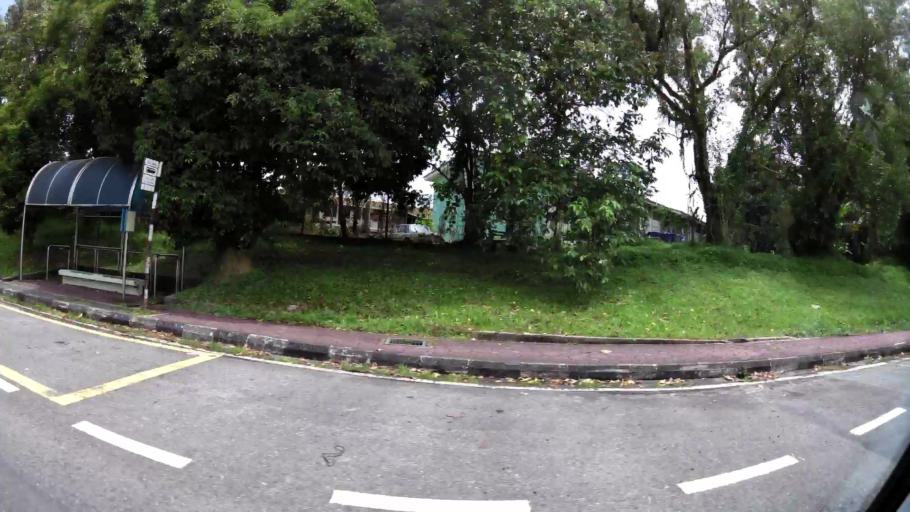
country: BN
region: Brunei and Muara
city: Bandar Seri Begawan
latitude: 4.9040
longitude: 114.9169
